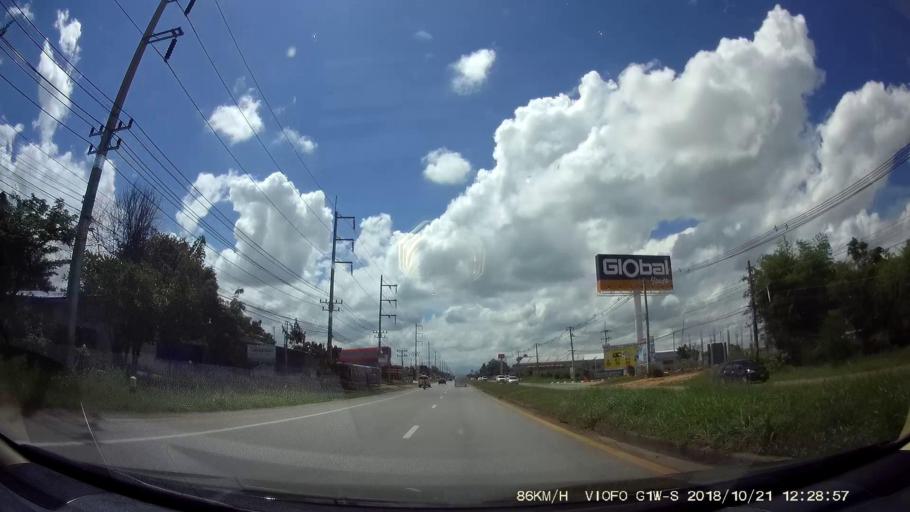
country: TH
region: Nakhon Ratchasima
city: Dan Khun Thot
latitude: 15.1844
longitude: 101.7564
